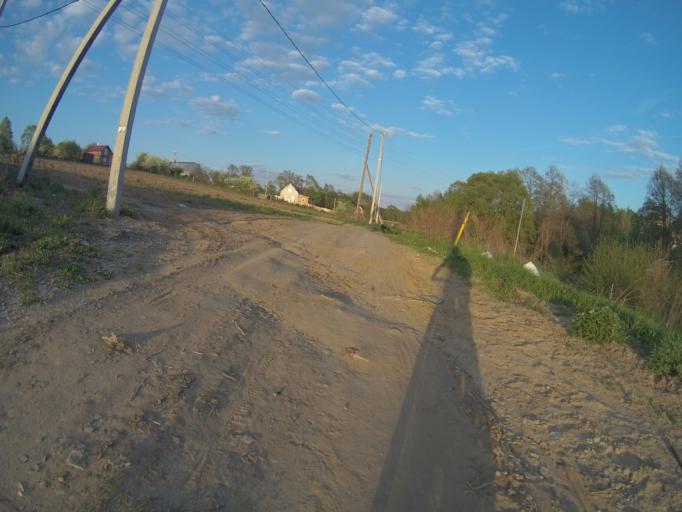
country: RU
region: Vladimir
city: Kommunar
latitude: 56.0656
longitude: 40.4847
